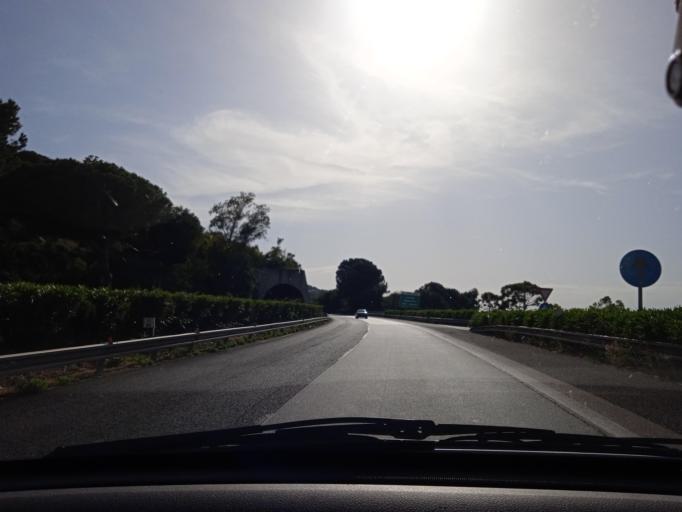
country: IT
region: Sicily
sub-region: Messina
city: Naso
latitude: 38.1509
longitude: 14.7706
